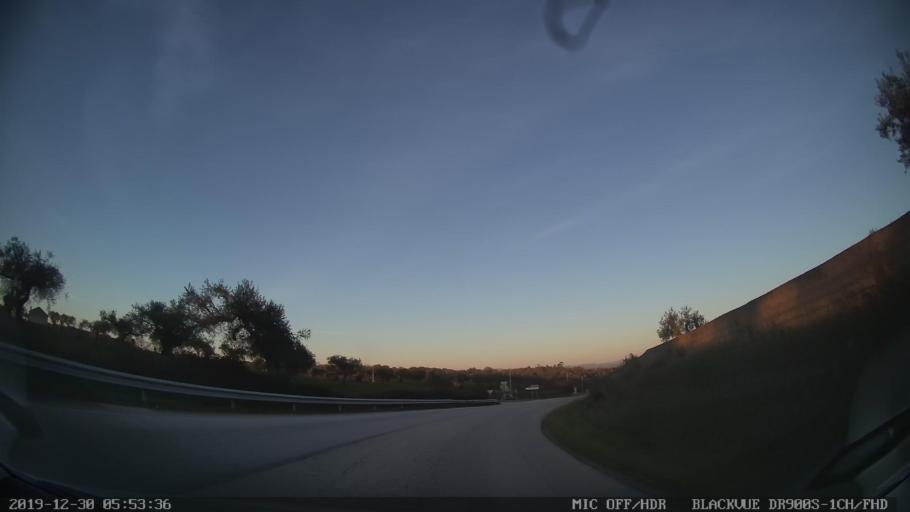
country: PT
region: Castelo Branco
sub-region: Idanha-A-Nova
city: Idanha-a-Nova
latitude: 40.0171
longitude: -7.2517
